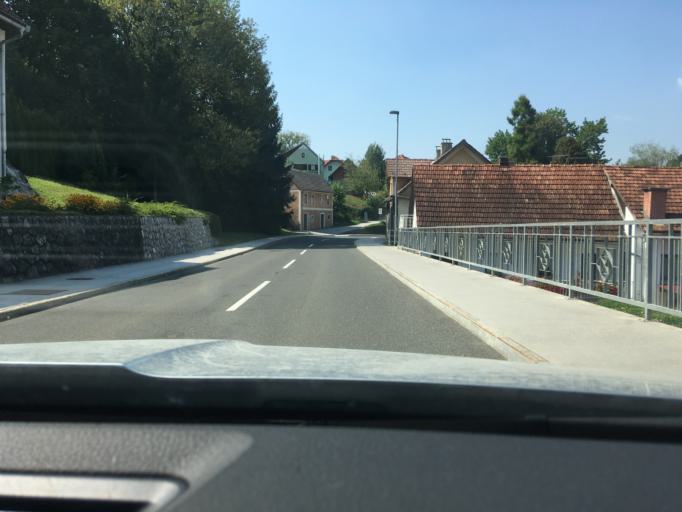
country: SI
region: Metlika
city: Metlika
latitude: 45.6490
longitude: 15.3172
